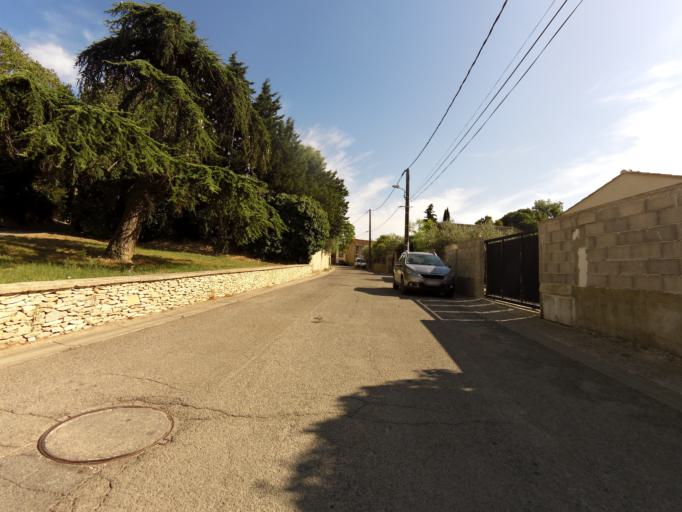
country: FR
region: Languedoc-Roussillon
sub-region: Departement du Gard
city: Gallargues-le-Montueux
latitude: 43.7234
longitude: 4.1701
